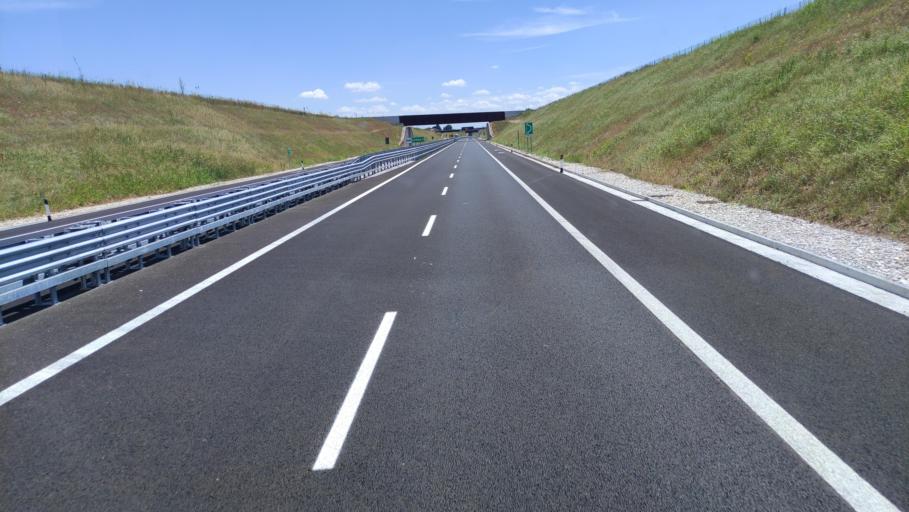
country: IT
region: Veneto
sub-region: Provincia di Treviso
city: Altivole
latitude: 45.7419
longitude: 11.9369
